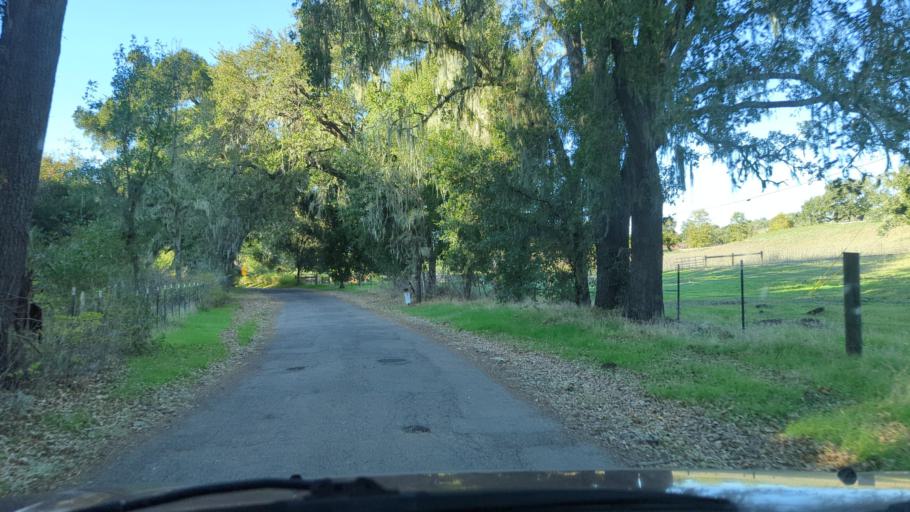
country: US
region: California
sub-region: Santa Barbara County
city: Santa Ynez
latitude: 34.5687
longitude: -120.0958
